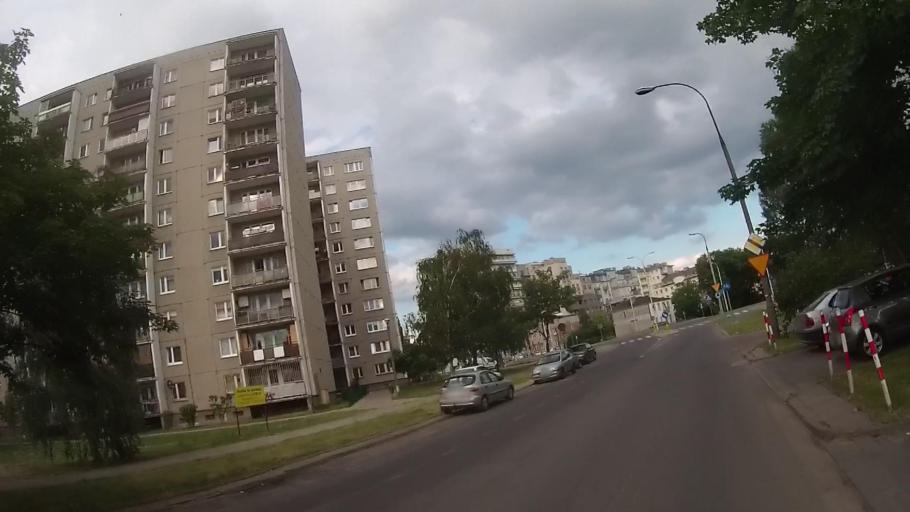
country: PL
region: Masovian Voivodeship
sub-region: Warszawa
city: Praga Poludnie
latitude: 52.2335
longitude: 21.0828
